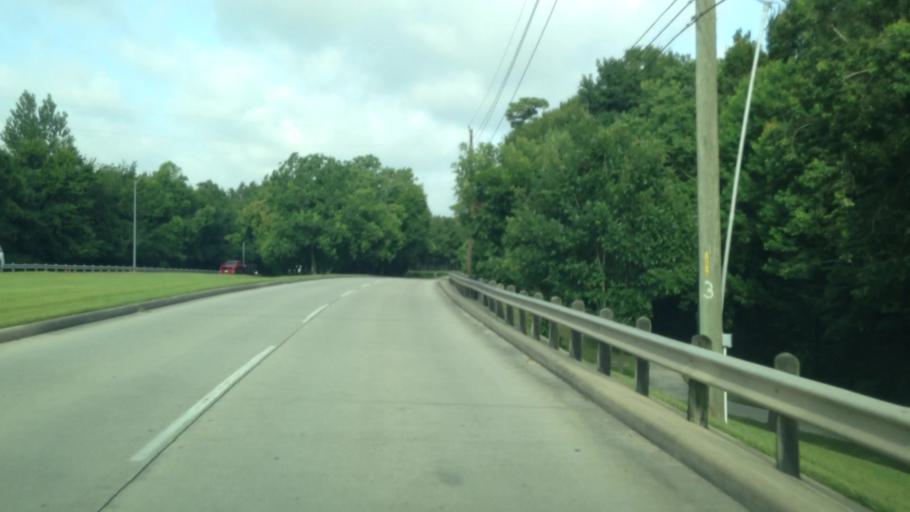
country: US
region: Texas
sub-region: Harris County
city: Atascocita
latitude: 29.9251
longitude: -95.1829
